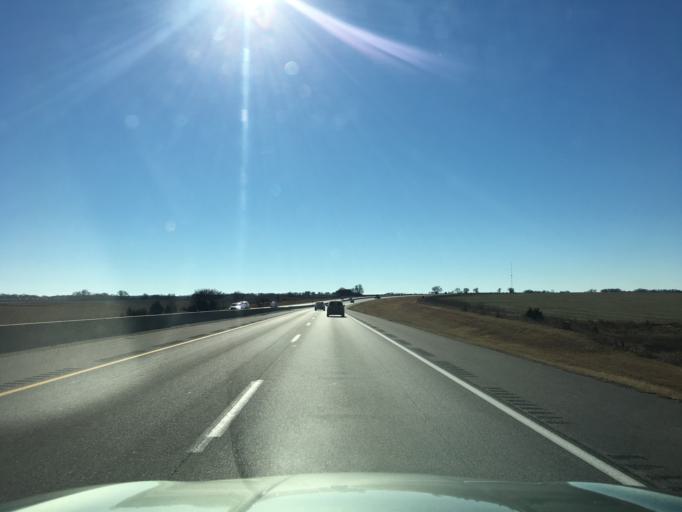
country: US
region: Kansas
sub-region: Sumner County
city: Belle Plaine
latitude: 37.3498
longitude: -97.3221
